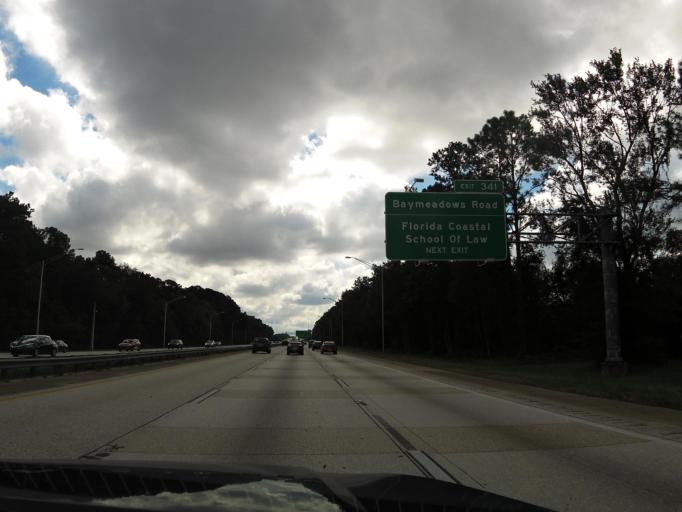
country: US
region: Florida
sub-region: Duval County
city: Jacksonville
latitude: 30.2270
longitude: -81.5766
